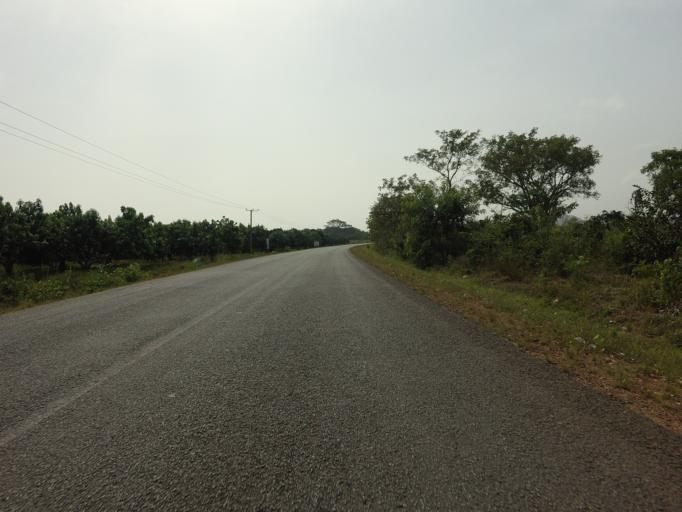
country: GH
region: Volta
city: Ho
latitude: 6.4026
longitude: 0.1776
